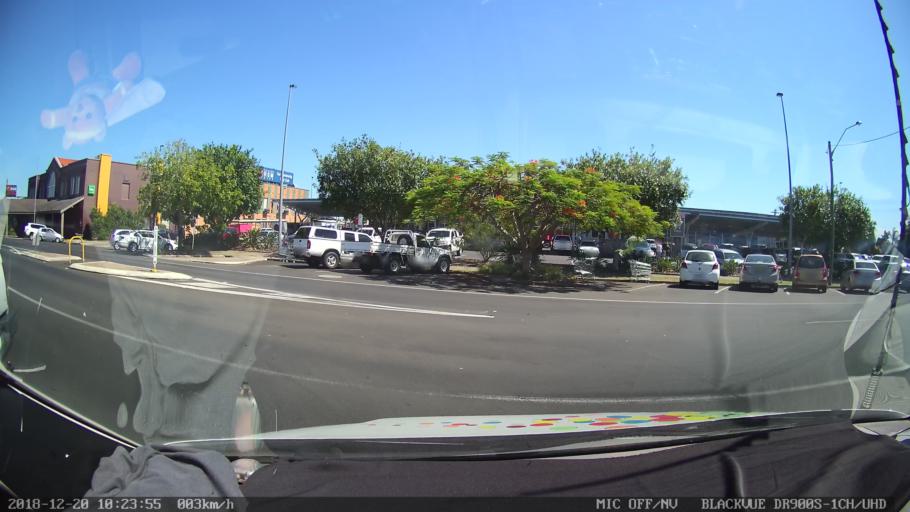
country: AU
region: New South Wales
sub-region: Richmond Valley
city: Casino
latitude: -28.8635
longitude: 153.0497
